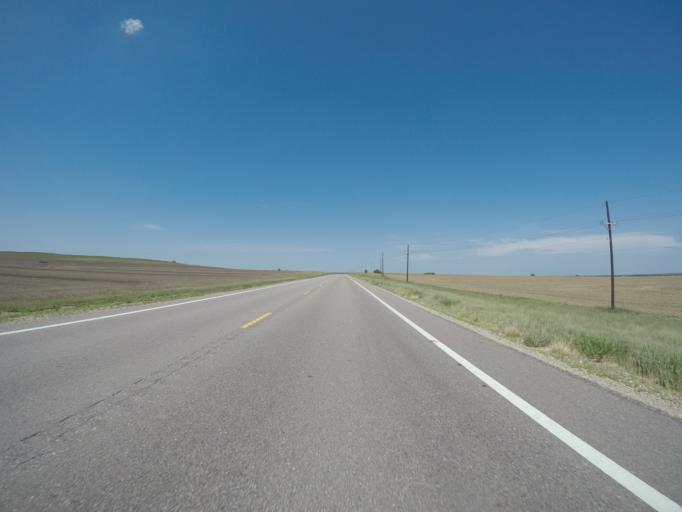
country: US
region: Kansas
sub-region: Osborne County
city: Osborne
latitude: 39.5101
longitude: -98.6765
